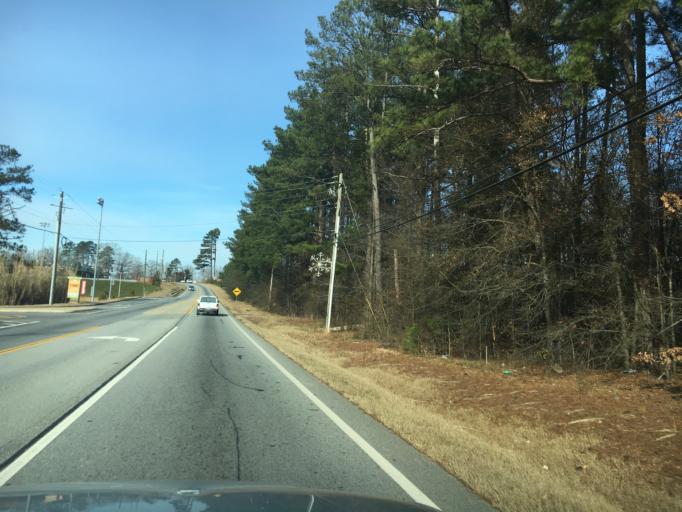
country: US
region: Georgia
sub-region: Jackson County
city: Hoschton
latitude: 34.1020
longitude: -83.7618
